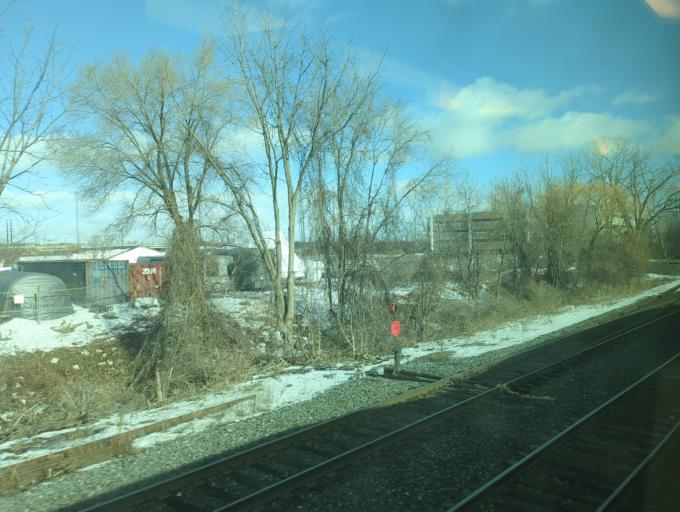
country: CA
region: Ontario
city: Burlington
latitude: 43.3384
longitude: -79.8137
